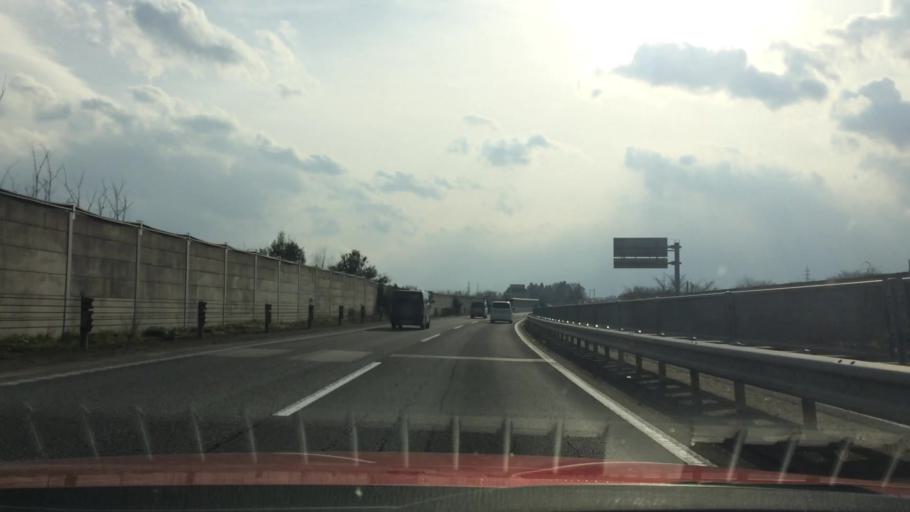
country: JP
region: Nagano
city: Tatsuno
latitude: 35.9388
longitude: 137.9812
